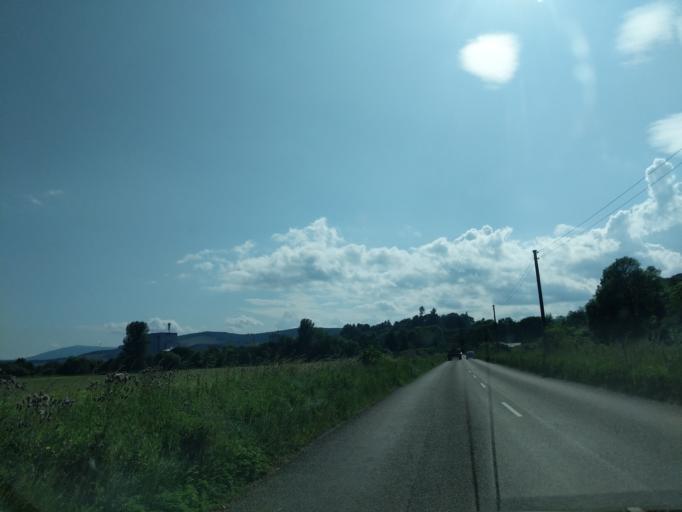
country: GB
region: Scotland
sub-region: Moray
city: Rothes
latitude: 57.5370
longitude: -3.2039
